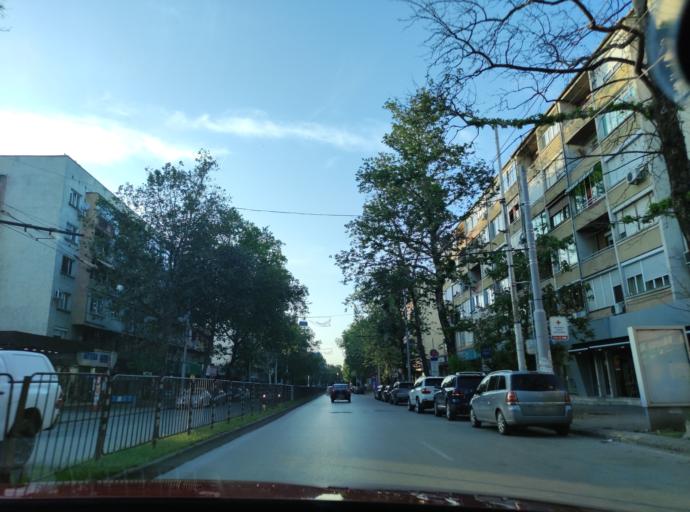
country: BG
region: Pleven
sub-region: Obshtina Pleven
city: Pleven
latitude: 43.4137
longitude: 24.6168
